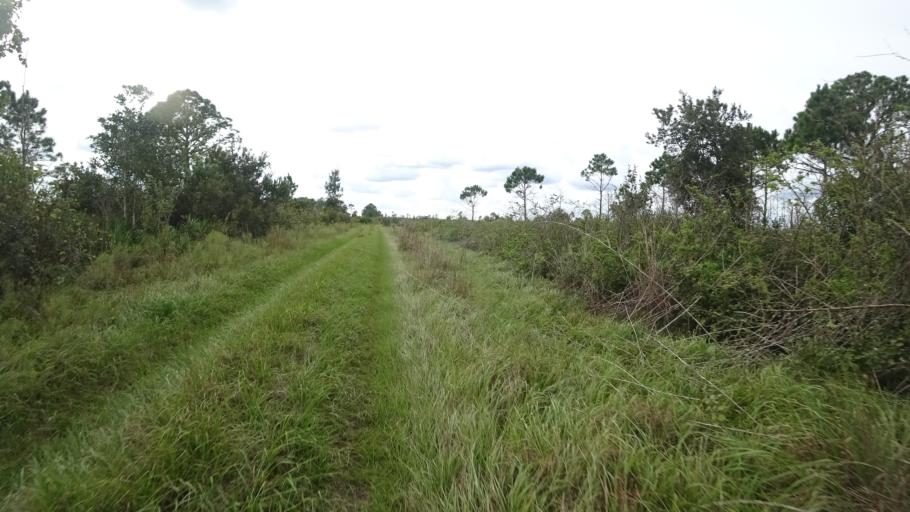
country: US
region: Florida
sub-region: Hillsborough County
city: Wimauma
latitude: 27.5589
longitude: -82.1258
